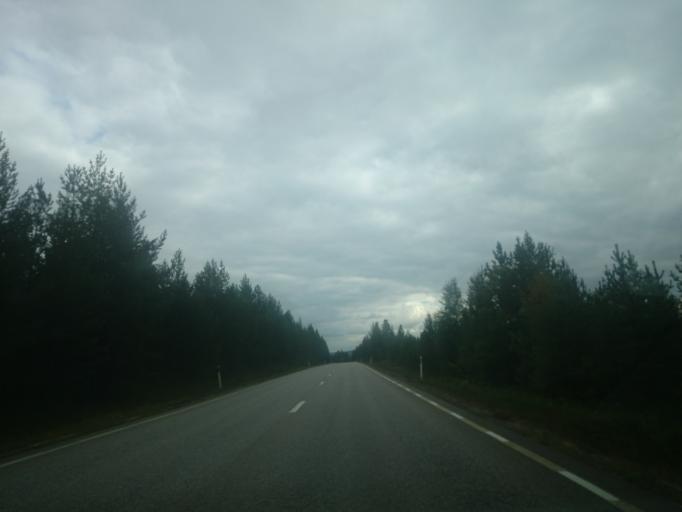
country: SE
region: Jaemtland
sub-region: Harjedalens Kommun
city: Sveg
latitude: 62.0539
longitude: 14.3054
